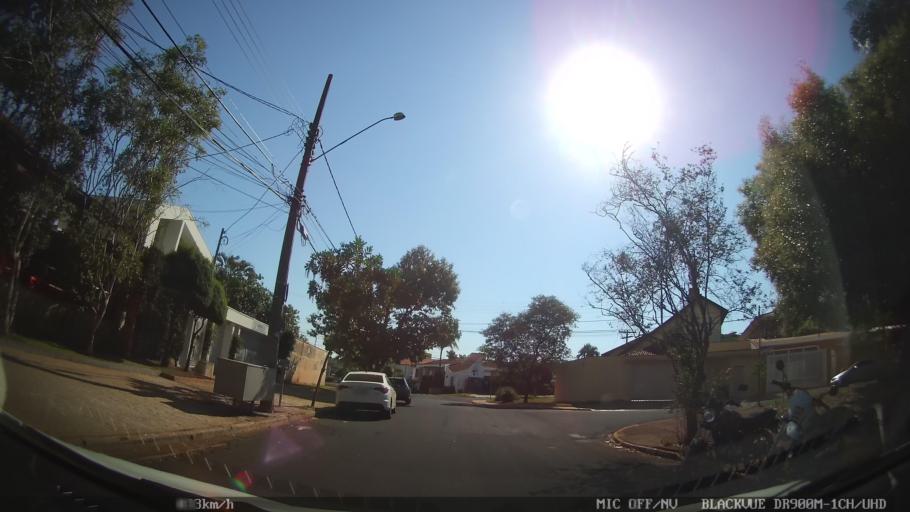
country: BR
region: Sao Paulo
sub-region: Ribeirao Preto
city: Ribeirao Preto
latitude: -21.1996
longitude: -47.8142
